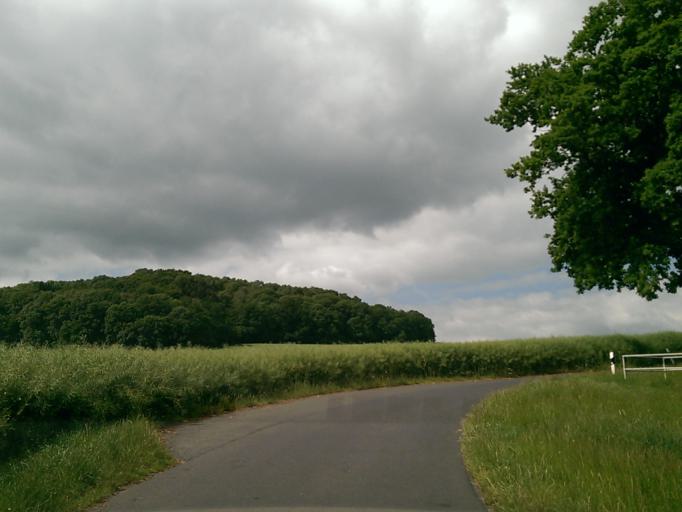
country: DE
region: Saxony
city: Eibau
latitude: 50.9701
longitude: 14.6906
